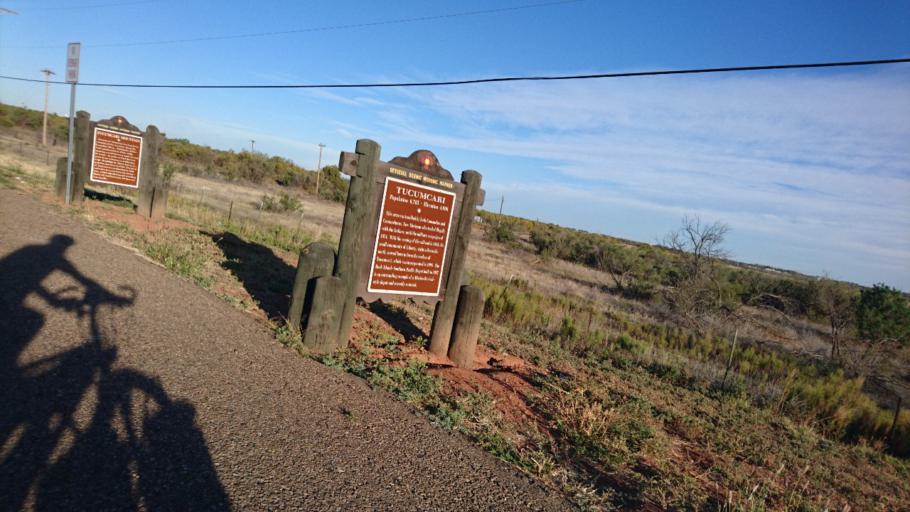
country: US
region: New Mexico
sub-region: Quay County
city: Tucumcari
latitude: 35.1721
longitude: -103.6938
